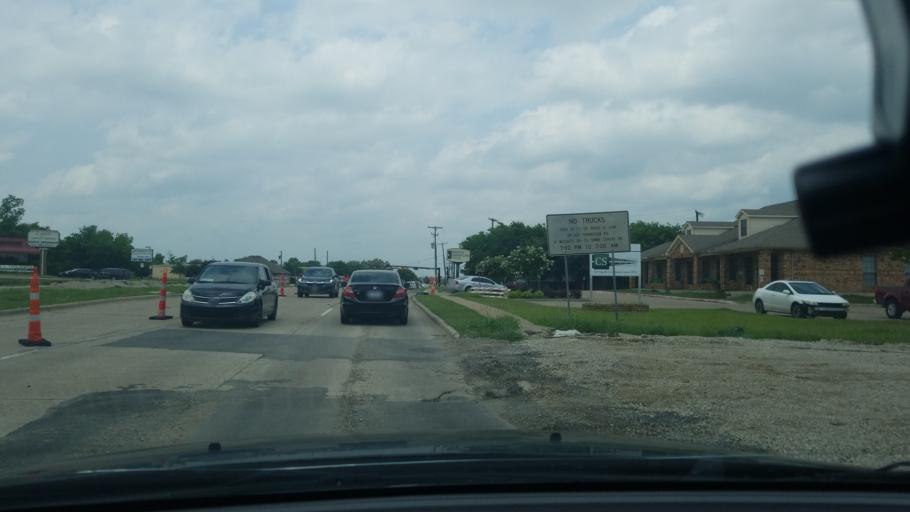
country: US
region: Texas
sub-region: Dallas County
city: Mesquite
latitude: 32.7970
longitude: -96.6340
